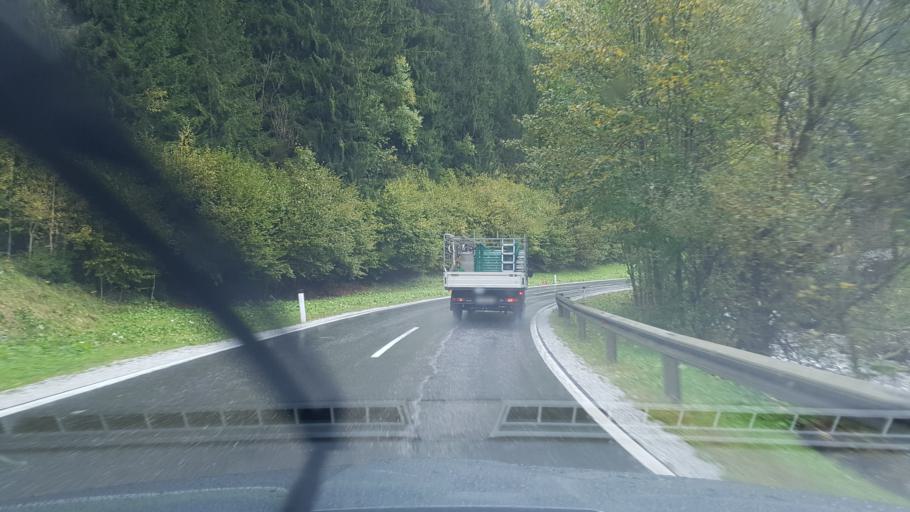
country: AT
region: Styria
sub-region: Politischer Bezirk Voitsberg
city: Salla
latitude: 47.1130
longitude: 14.9905
